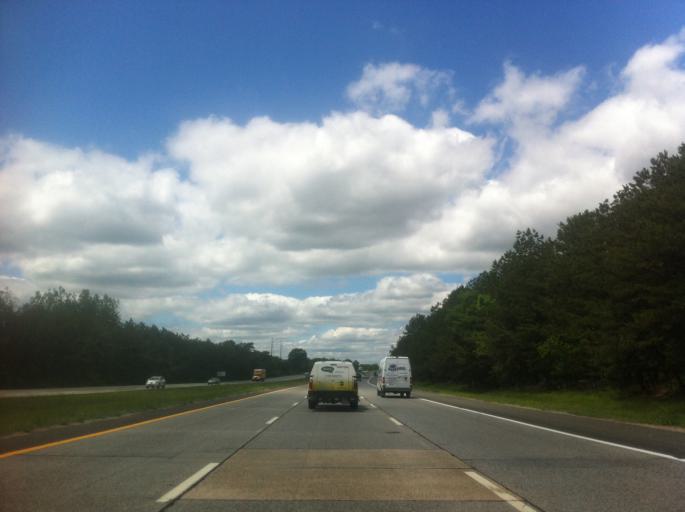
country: US
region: New York
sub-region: Suffolk County
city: Manorville
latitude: 40.8519
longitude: -72.8526
